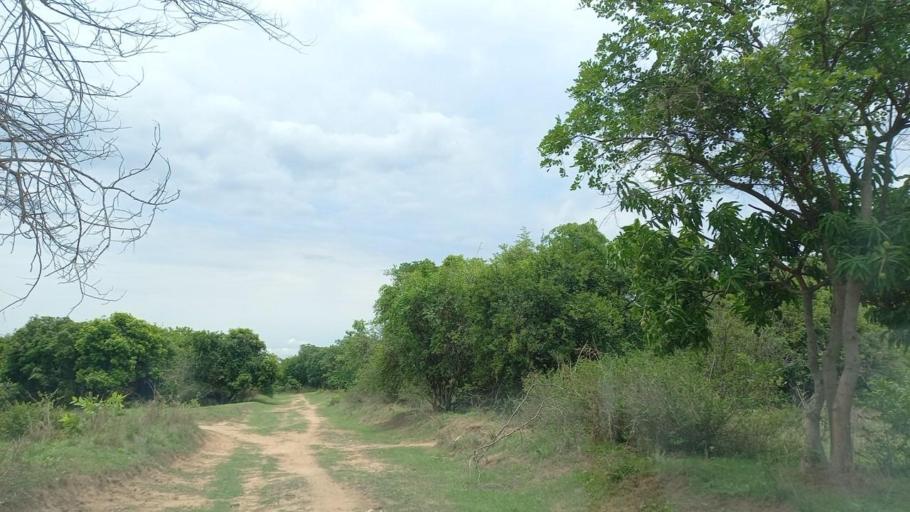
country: ZM
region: North-Western
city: Mufumbwe
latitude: -13.6936
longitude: 24.9779
